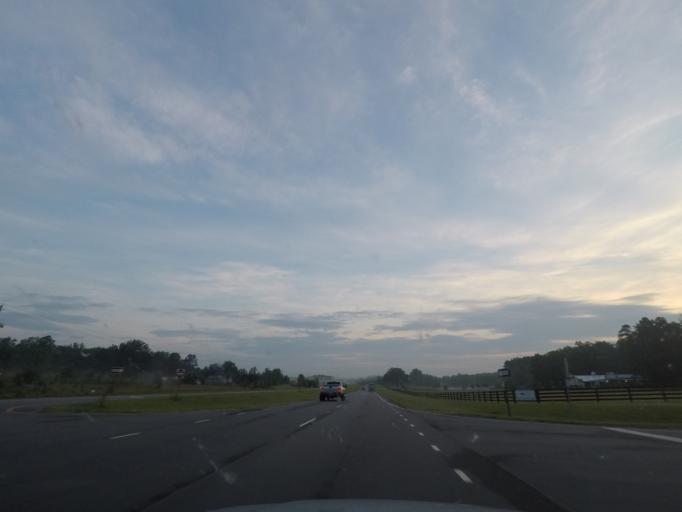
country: US
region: North Carolina
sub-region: Person County
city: Roxboro
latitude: 36.2315
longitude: -78.9316
